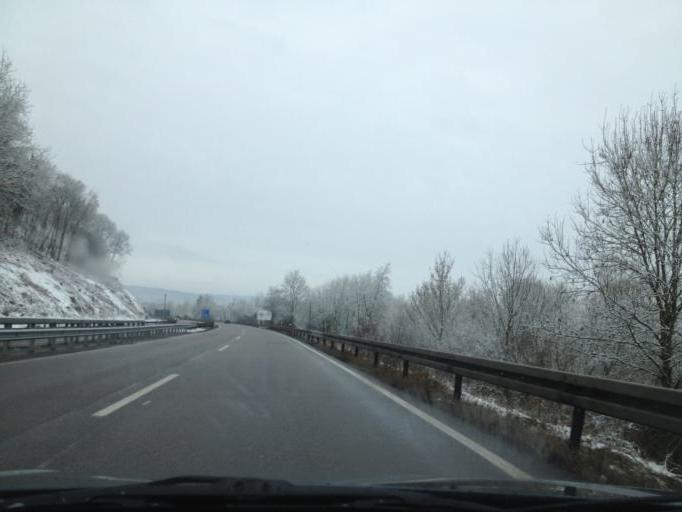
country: DE
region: Rheinland-Pfalz
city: Zweibrucken
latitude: 49.2594
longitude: 7.3266
